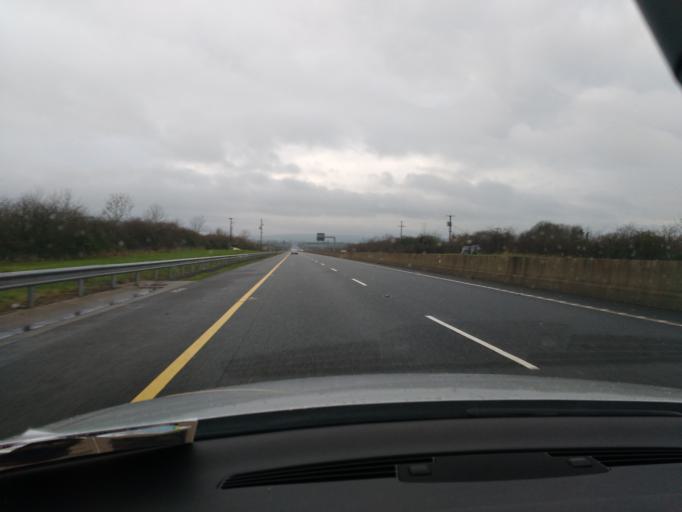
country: IE
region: Munster
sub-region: North Tipperary
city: Nenagh
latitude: 52.8488
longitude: -8.1669
